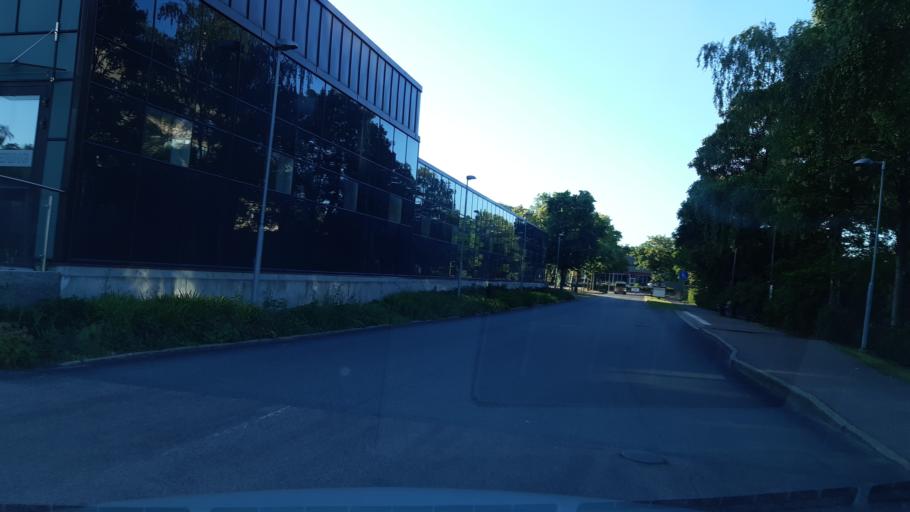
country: SE
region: Vaestra Goetaland
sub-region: Goteborg
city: Eriksbo
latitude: 57.7208
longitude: 12.0519
